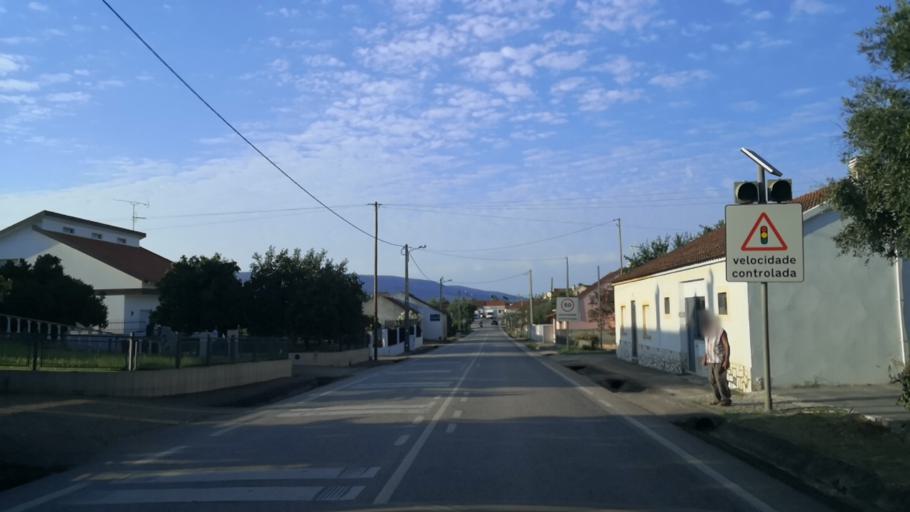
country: PT
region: Santarem
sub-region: Alcanena
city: Alcanena
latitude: 39.4488
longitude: -8.6227
